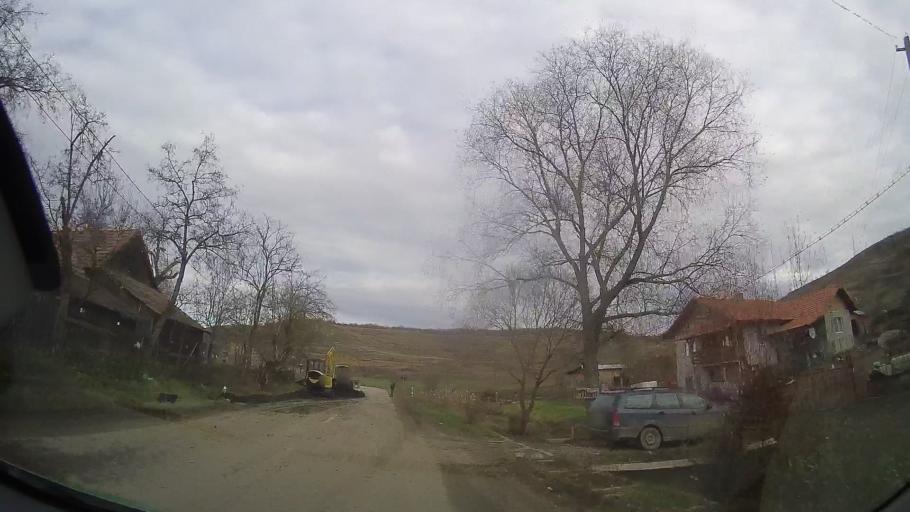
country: RO
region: Bistrita-Nasaud
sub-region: Comuna Micestii de Campie
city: Micestii de Campie
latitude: 46.8367
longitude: 24.3038
